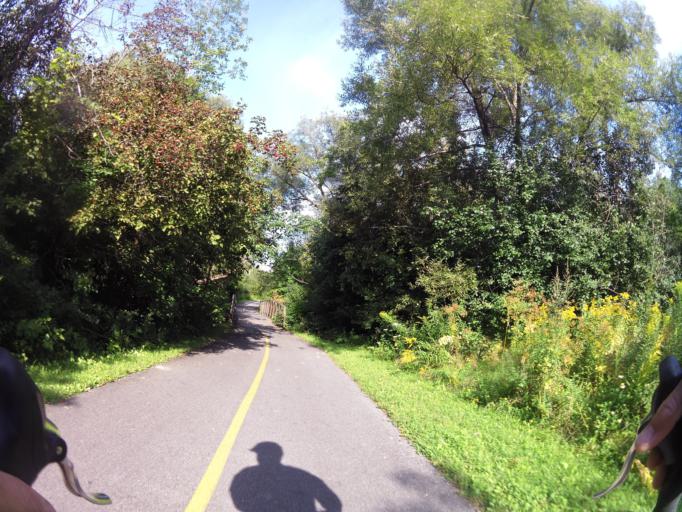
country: CA
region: Ontario
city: Bells Corners
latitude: 45.3417
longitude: -75.8736
